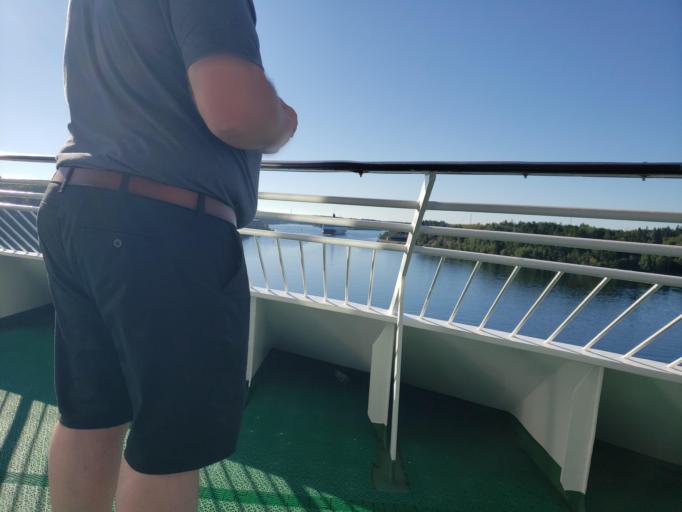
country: SE
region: Stockholm
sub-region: Vaxholms Kommun
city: Vaxholm
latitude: 59.4052
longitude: 18.4287
